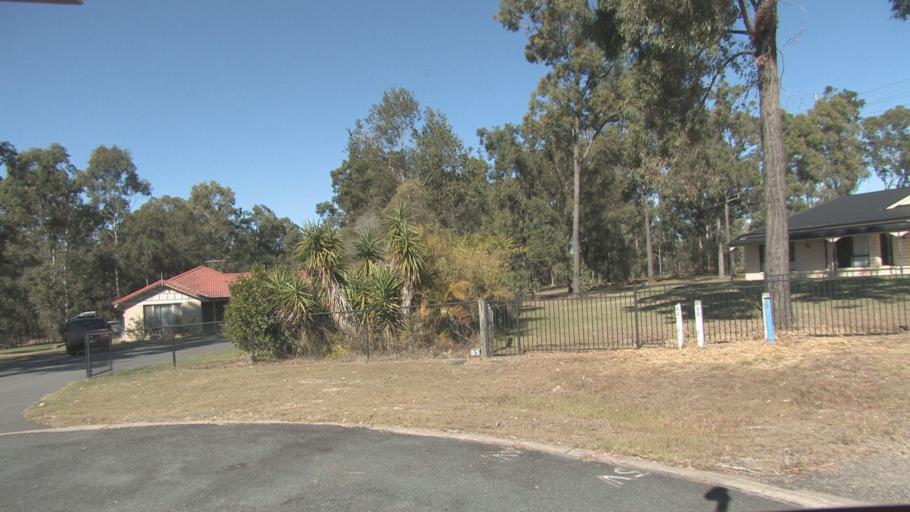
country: AU
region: Queensland
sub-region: Logan
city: North Maclean
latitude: -27.7344
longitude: 152.9656
